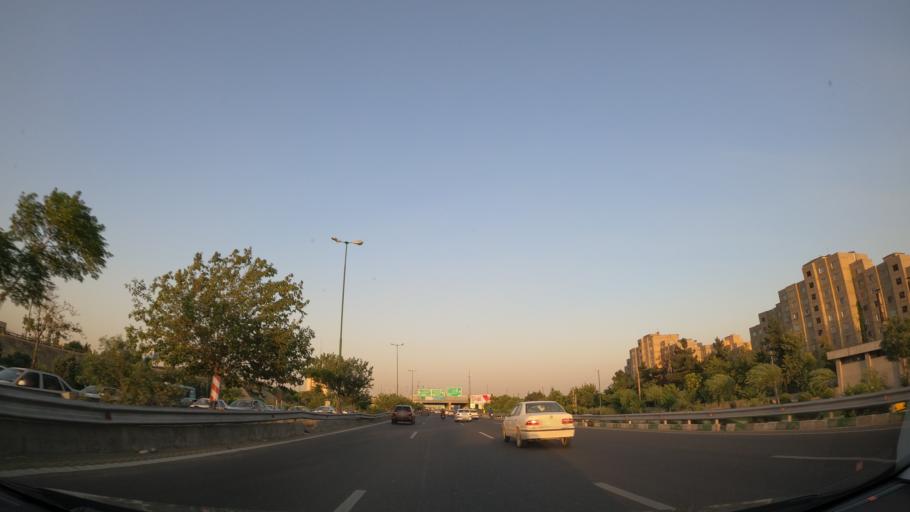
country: IR
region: Tehran
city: Tehran
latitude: 35.7142
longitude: 51.3263
